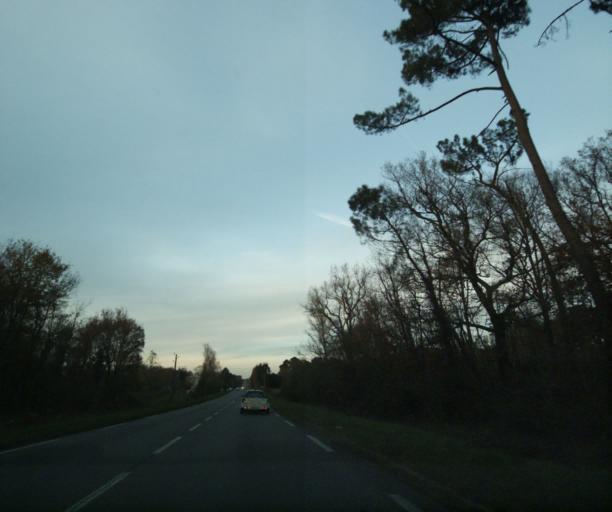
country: FR
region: Aquitaine
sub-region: Departement de la Gironde
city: Bazas
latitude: 44.4842
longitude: -0.2314
